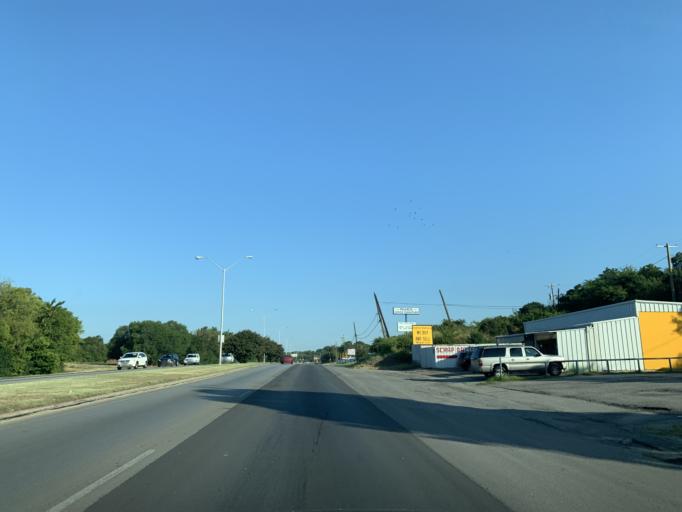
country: US
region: Texas
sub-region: Tarrant County
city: River Oaks
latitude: 32.7903
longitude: -97.3889
